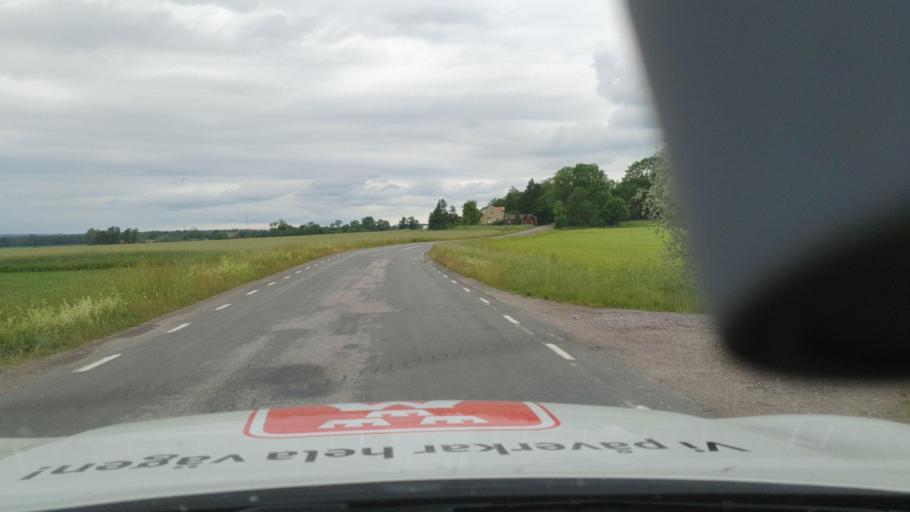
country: SE
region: Vaestra Goetaland
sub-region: Tidaholms Kommun
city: Olofstorp
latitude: 58.3319
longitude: 13.9881
